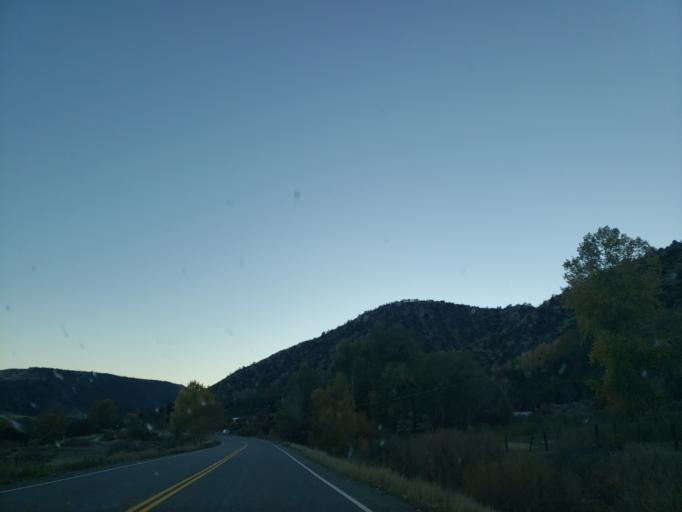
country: US
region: Colorado
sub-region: Garfield County
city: New Castle
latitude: 39.5661
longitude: -107.5508
